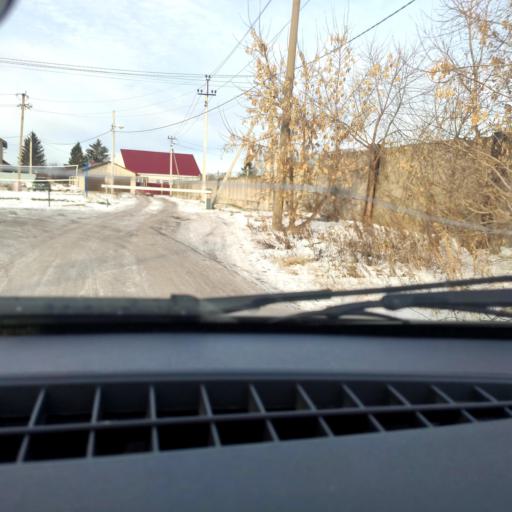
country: RU
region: Bashkortostan
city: Avdon
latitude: 54.6885
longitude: 55.7920
